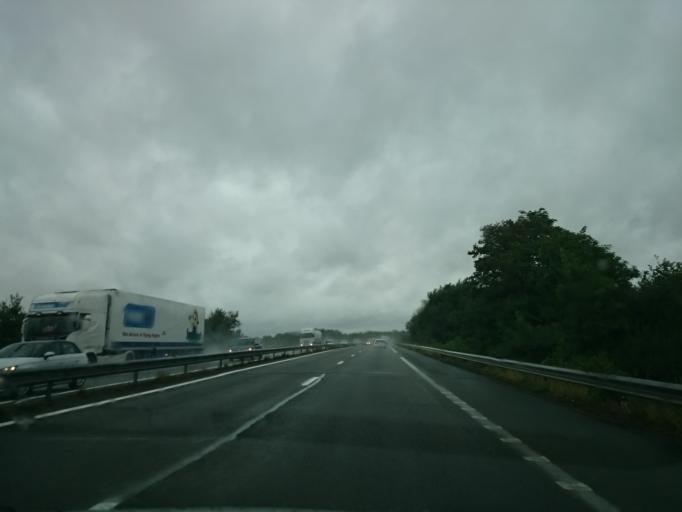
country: FR
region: Pays de la Loire
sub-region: Departement de la Loire-Atlantique
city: Heric
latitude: 47.4554
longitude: -1.6405
